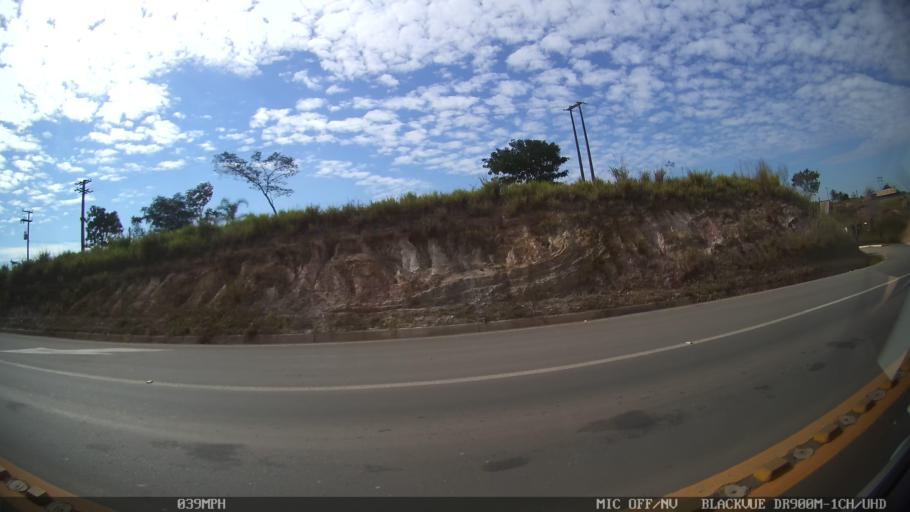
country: BR
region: Sao Paulo
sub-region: Santa Barbara D'Oeste
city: Santa Barbara d'Oeste
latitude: -22.7030
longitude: -47.4569
